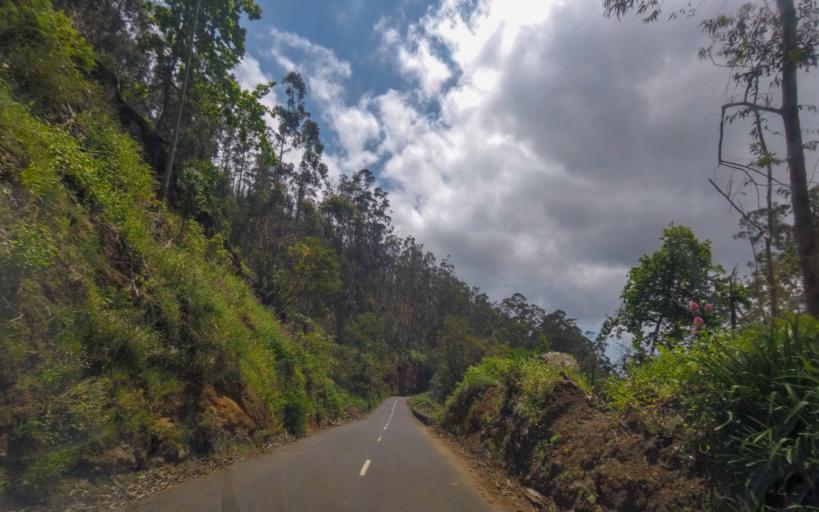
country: PT
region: Madeira
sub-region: Funchal
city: Nossa Senhora do Monte
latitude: 32.6793
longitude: -16.8802
